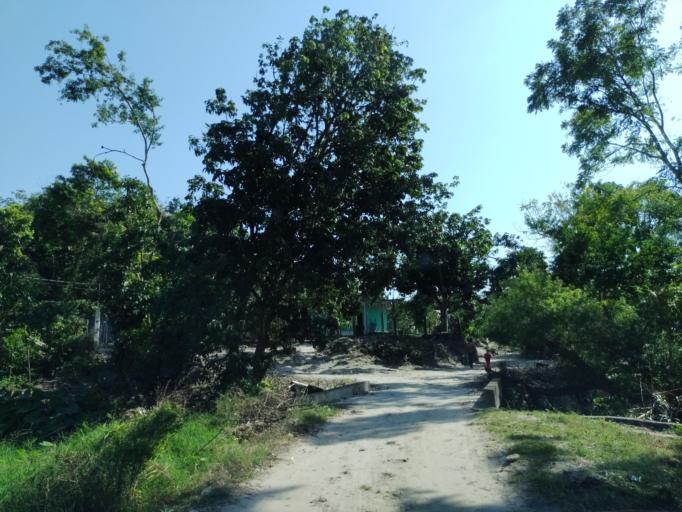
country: MX
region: Veracruz
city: Agua Dulce
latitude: 20.2563
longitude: -97.2511
